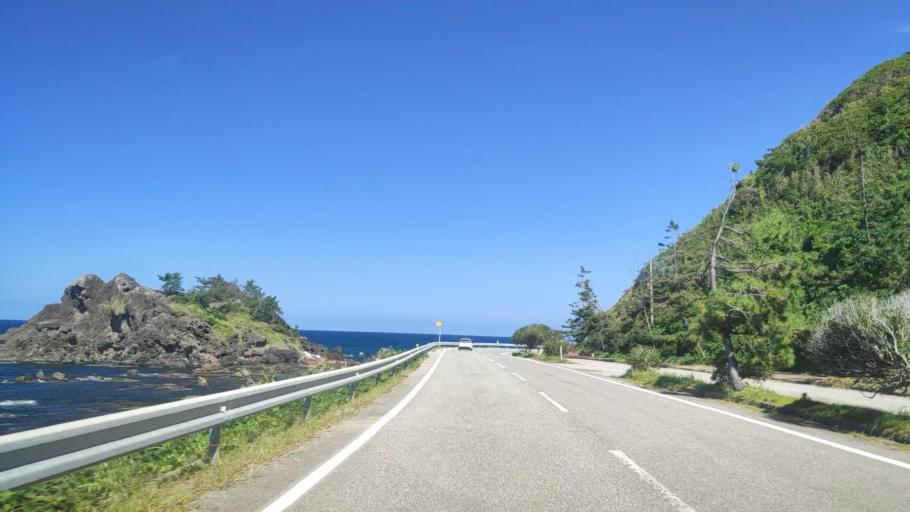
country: JP
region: Ishikawa
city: Nanao
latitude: 37.5066
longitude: 137.1999
